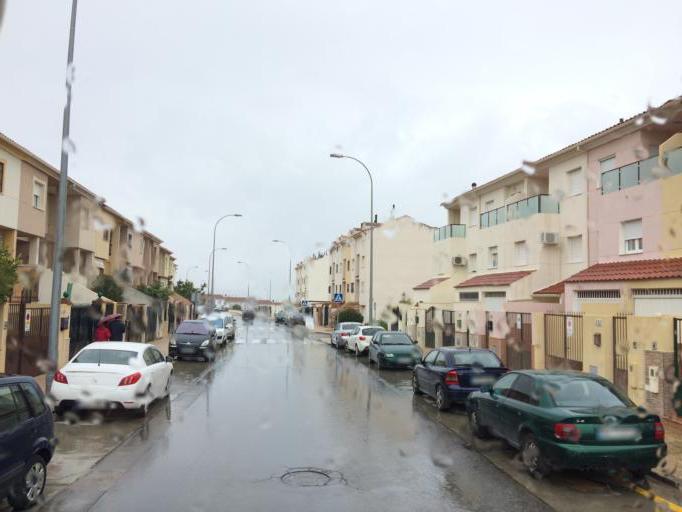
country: ES
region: Andalusia
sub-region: Provincia de Malaga
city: Antequera
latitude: 37.0250
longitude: -4.5527
